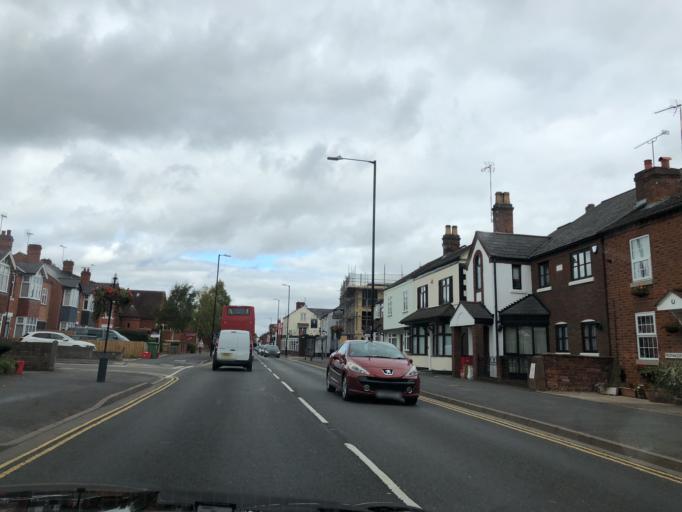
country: GB
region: England
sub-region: Warwickshire
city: Kenilworth
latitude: 52.3382
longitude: -1.5746
